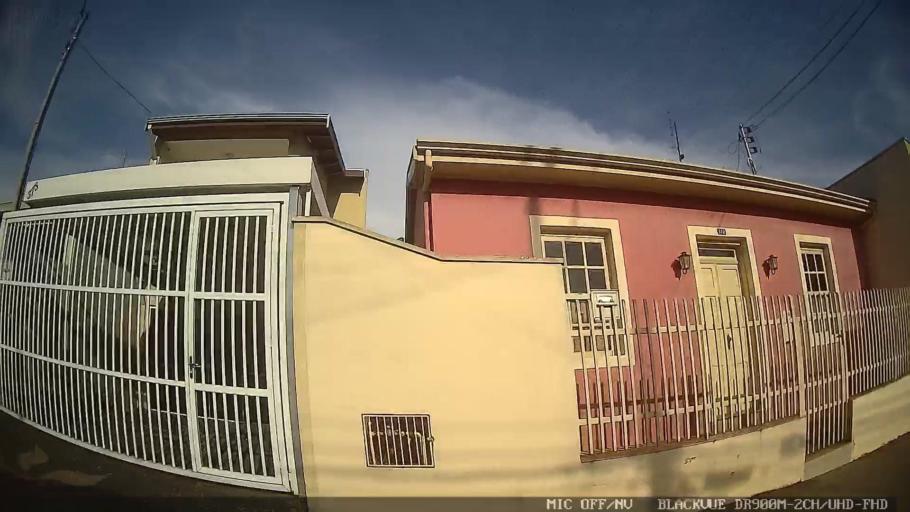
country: BR
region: Sao Paulo
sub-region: Tiete
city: Tiete
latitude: -23.0925
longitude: -47.7179
